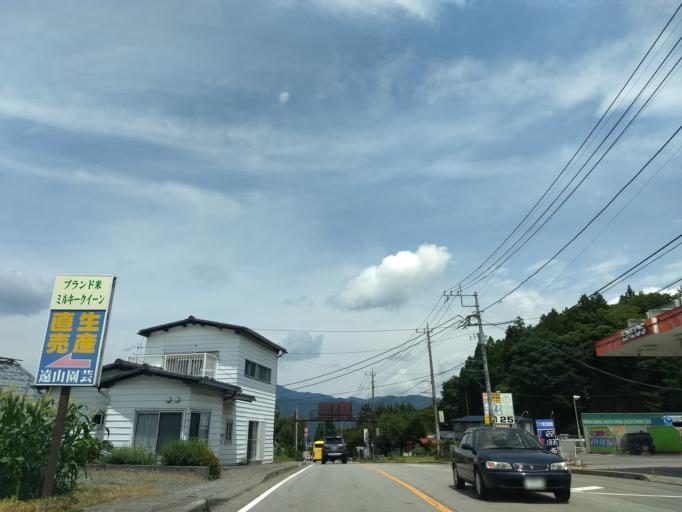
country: JP
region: Yamanashi
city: Fujikawaguchiko
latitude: 35.4674
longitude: 138.8017
